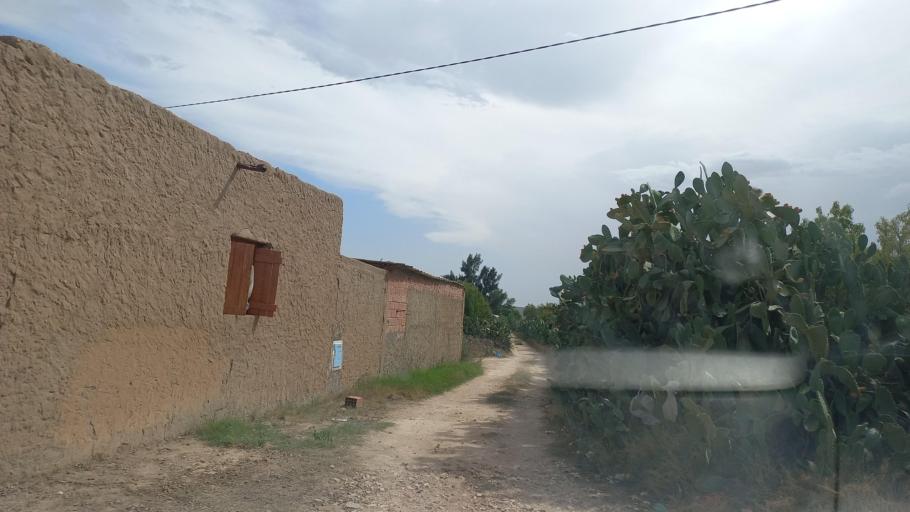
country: TN
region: Al Qasrayn
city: Kasserine
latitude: 35.2481
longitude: 9.0109
